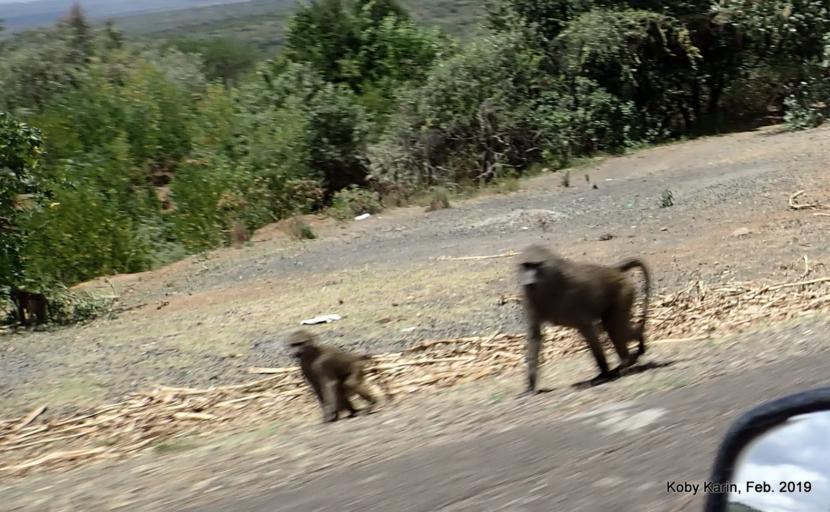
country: KE
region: Narok
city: Narok
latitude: -1.1138
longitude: 36.0457
